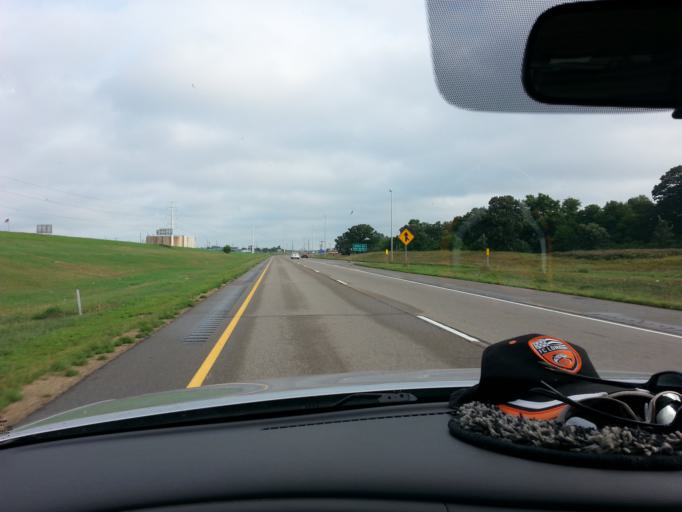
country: US
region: Minnesota
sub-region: Dakota County
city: Inver Grove Heights
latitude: 44.7662
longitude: -93.0339
